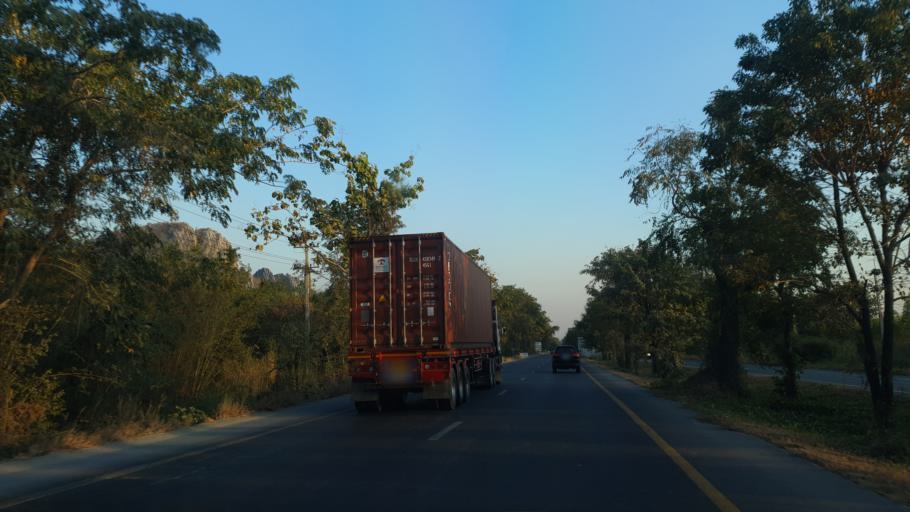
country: TH
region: Nakhon Sawan
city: Banphot Phisai
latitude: 15.9319
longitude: 99.8692
